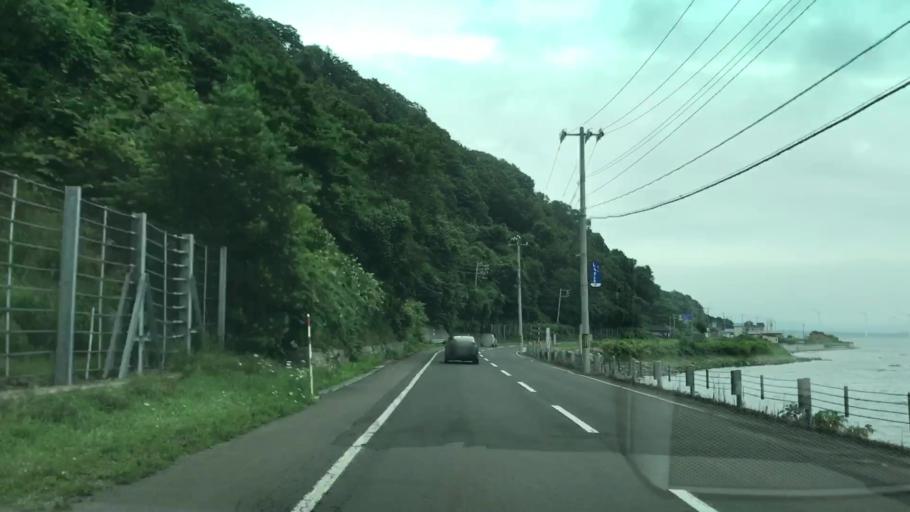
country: JP
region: Hokkaido
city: Iwanai
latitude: 42.7960
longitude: 140.3104
